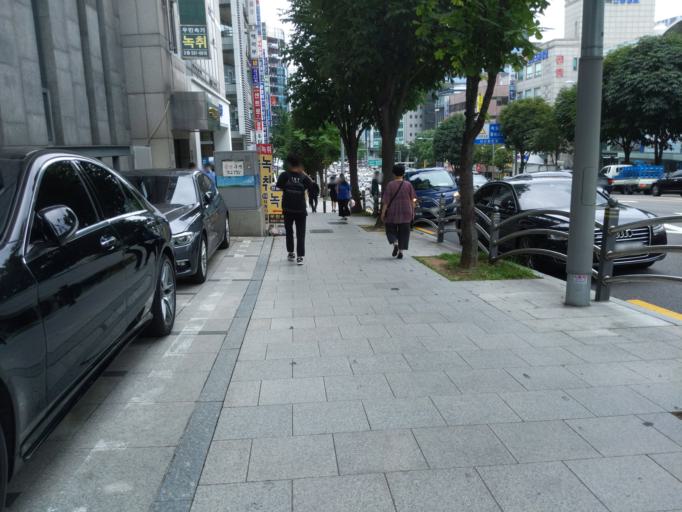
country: KR
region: Seoul
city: Seoul
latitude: 37.4955
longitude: 127.0134
